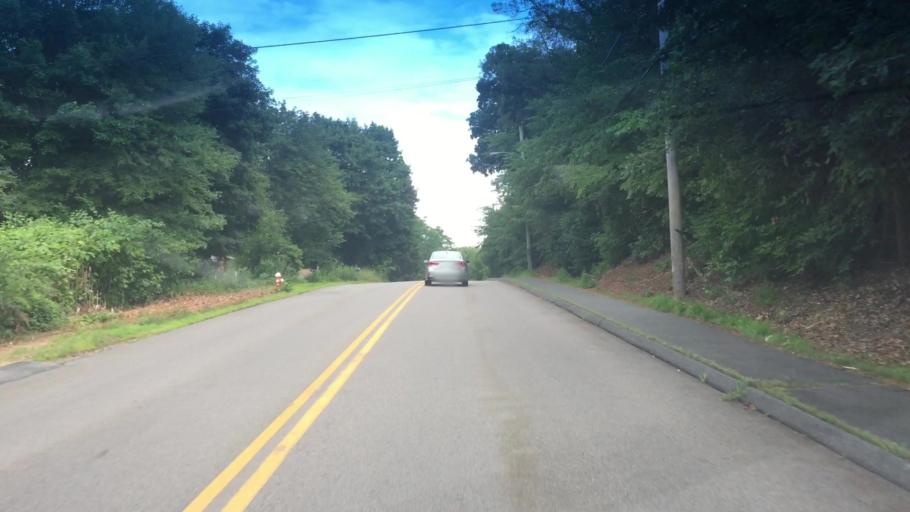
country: US
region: Massachusetts
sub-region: Norfolk County
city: Medway
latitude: 42.1187
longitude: -71.3964
